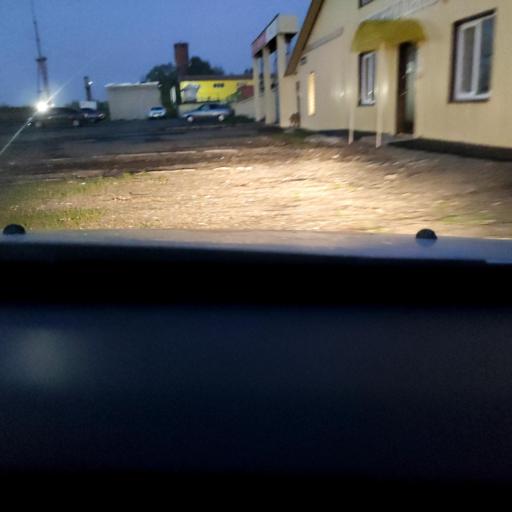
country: RU
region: Perm
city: Kondratovo
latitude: 58.0097
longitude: 56.1037
